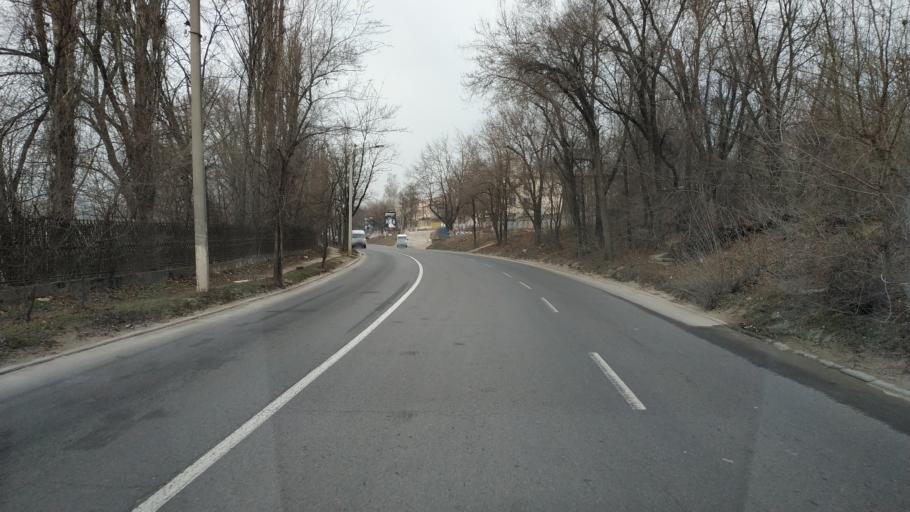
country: MD
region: Chisinau
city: Chisinau
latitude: 47.0528
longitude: 28.8157
